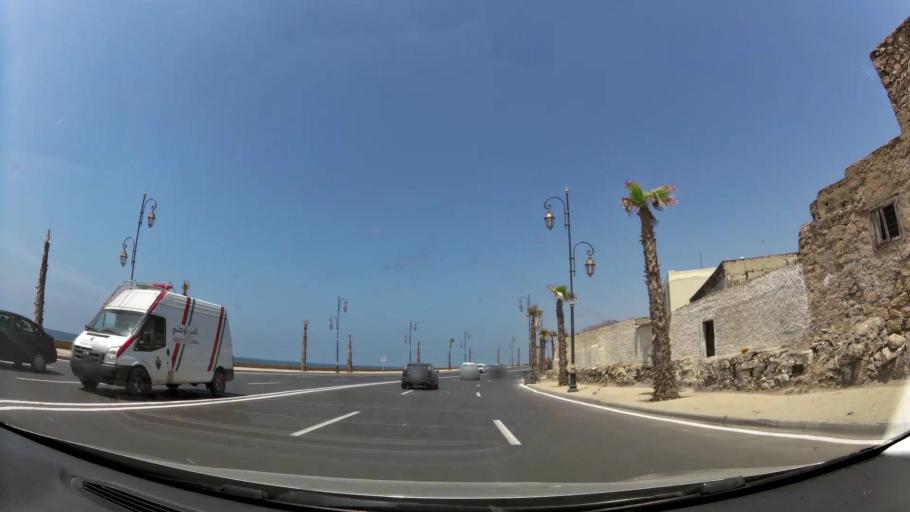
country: MA
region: Rabat-Sale-Zemmour-Zaer
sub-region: Rabat
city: Rabat
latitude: 34.0172
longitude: -6.8589
